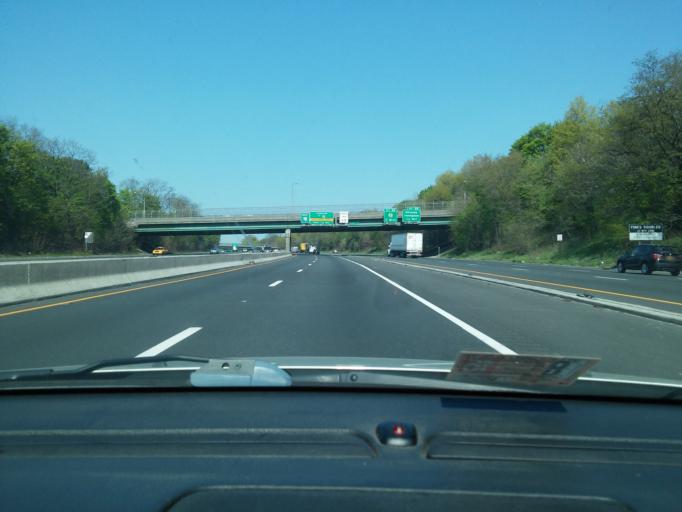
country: US
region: New Jersey
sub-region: Union County
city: Hillside
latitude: 40.7154
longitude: -74.2061
